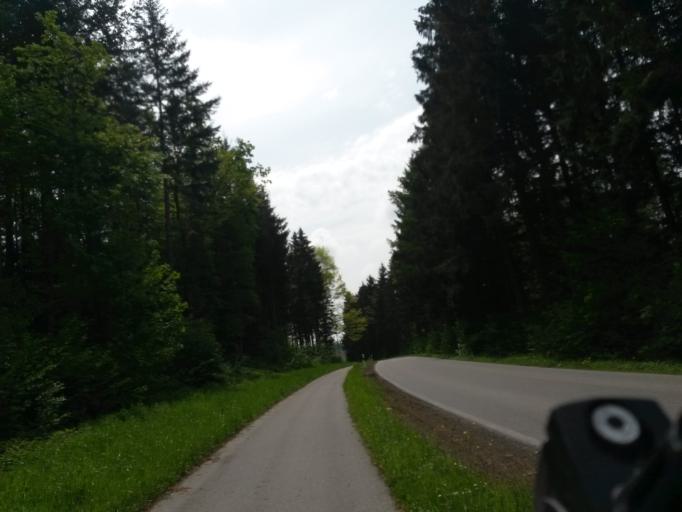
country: DE
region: Baden-Wuerttemberg
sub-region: Tuebingen Region
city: Bad Waldsee
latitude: 47.9539
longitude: 9.7396
